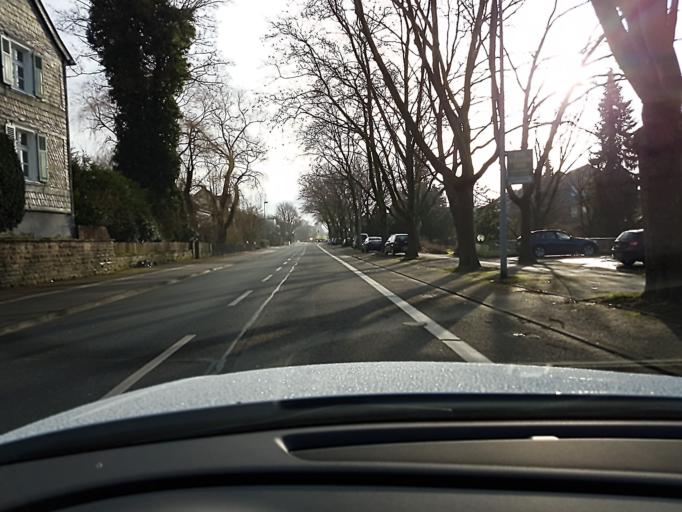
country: DE
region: North Rhine-Westphalia
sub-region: Regierungsbezirk Dusseldorf
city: Muelheim (Ruhr)
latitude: 51.4064
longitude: 6.8965
